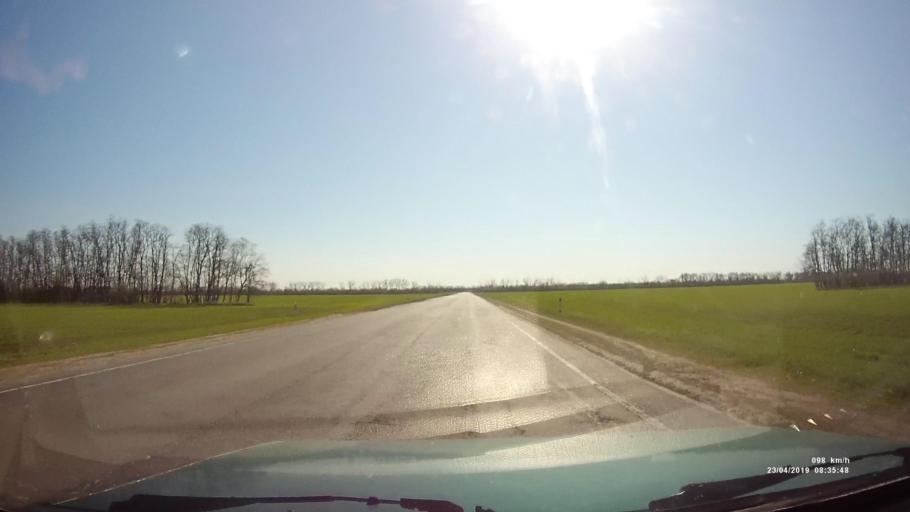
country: RU
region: Rostov
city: Tselina
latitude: 46.5221
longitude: 41.1405
